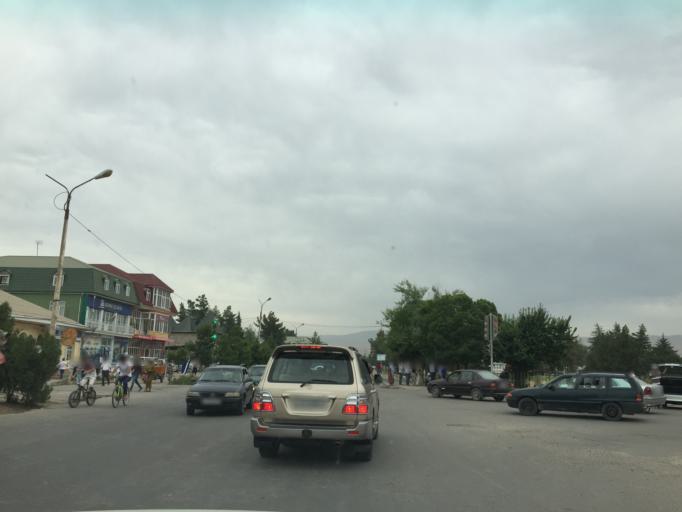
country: TJ
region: Khatlon
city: Vose'
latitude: 37.8055
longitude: 69.6420
